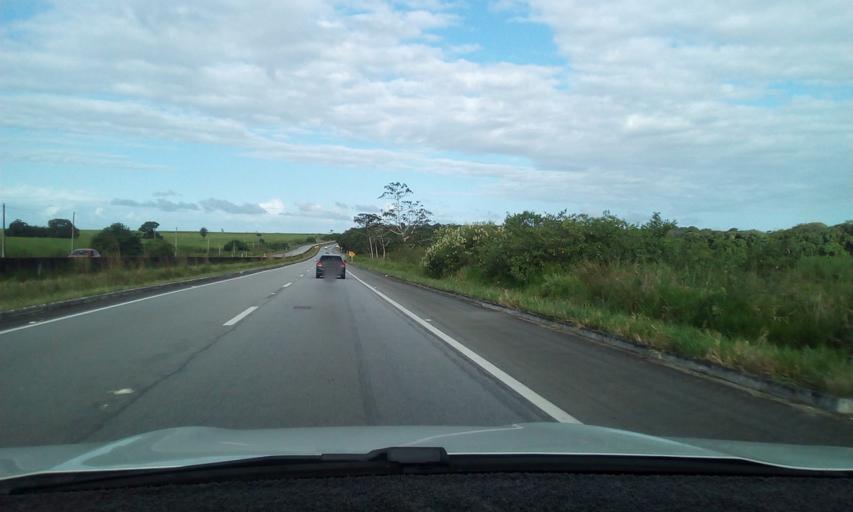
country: BR
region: Paraiba
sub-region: Santa Rita
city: Santa Rita
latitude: -7.0668
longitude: -35.0067
